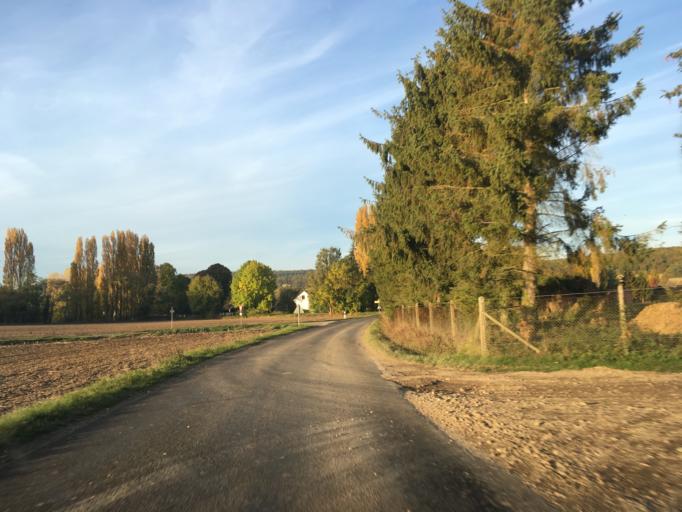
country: FR
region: Haute-Normandie
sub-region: Departement de l'Eure
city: Heudreville-sur-Eure
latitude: 49.1221
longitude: 1.2150
